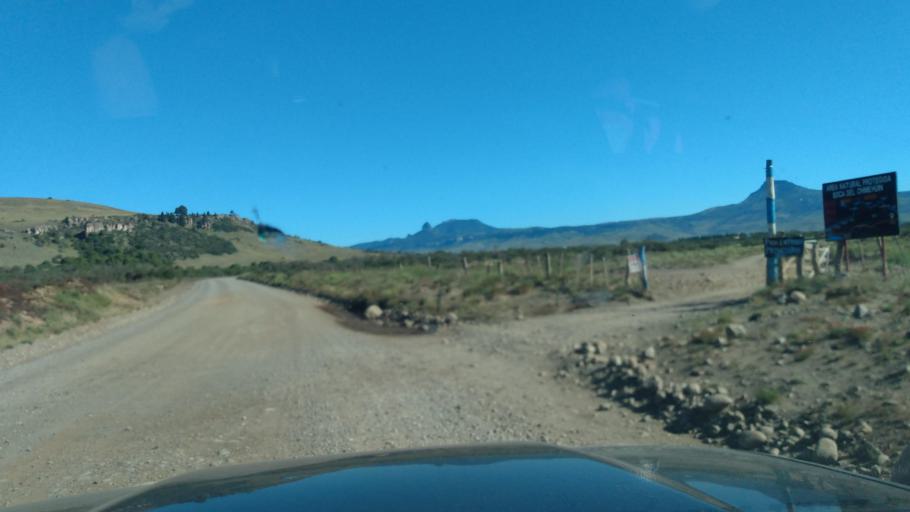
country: AR
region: Neuquen
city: Junin de los Andes
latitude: -39.8464
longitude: -71.1868
